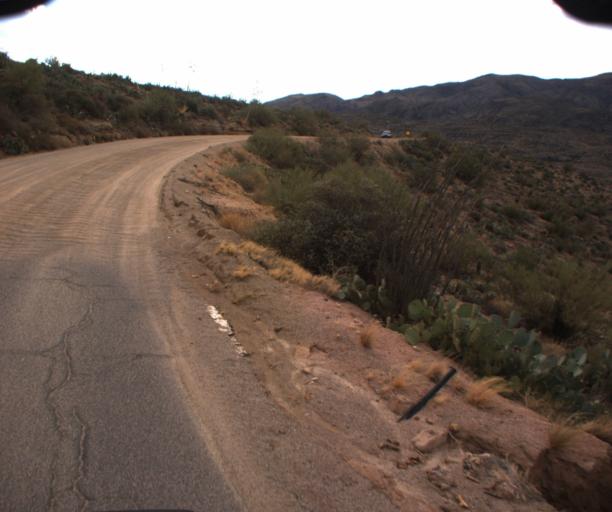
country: US
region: Arizona
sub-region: Pinal County
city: Gold Camp
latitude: 33.5377
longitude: -111.3251
